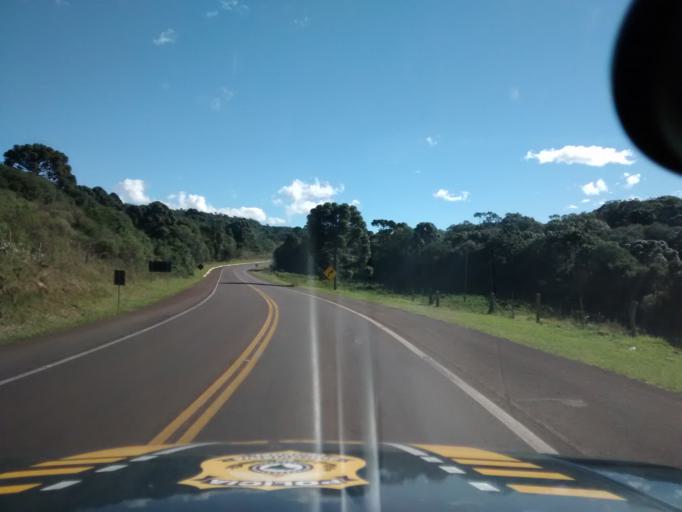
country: BR
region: Rio Grande do Sul
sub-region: Vacaria
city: Vacaria
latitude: -28.3312
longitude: -51.1614
